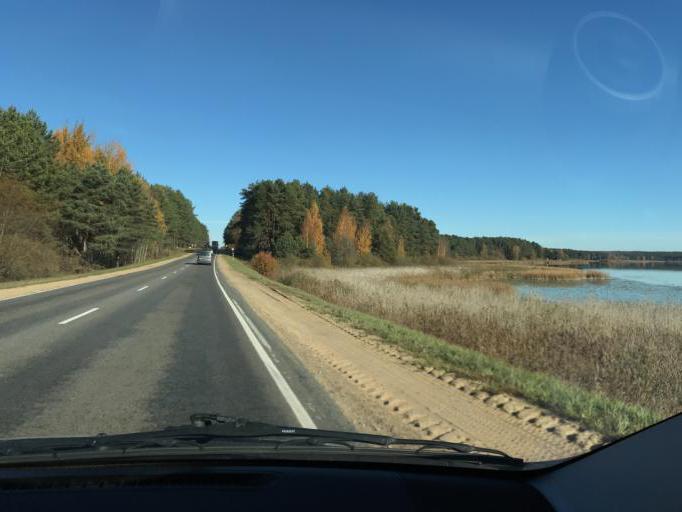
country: BY
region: Vitebsk
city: Polatsk
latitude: 55.3161
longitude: 28.7767
